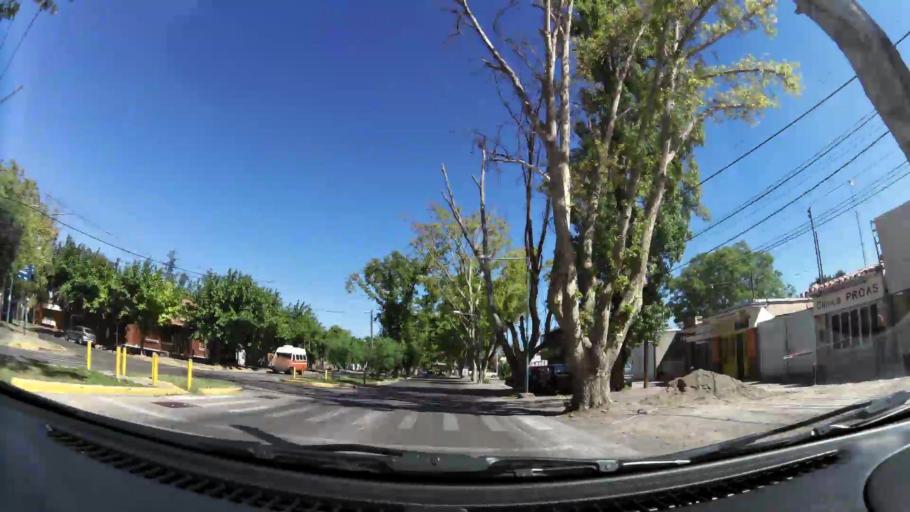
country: AR
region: Mendoza
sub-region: Departamento de Godoy Cruz
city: Godoy Cruz
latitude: -32.9412
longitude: -68.8272
